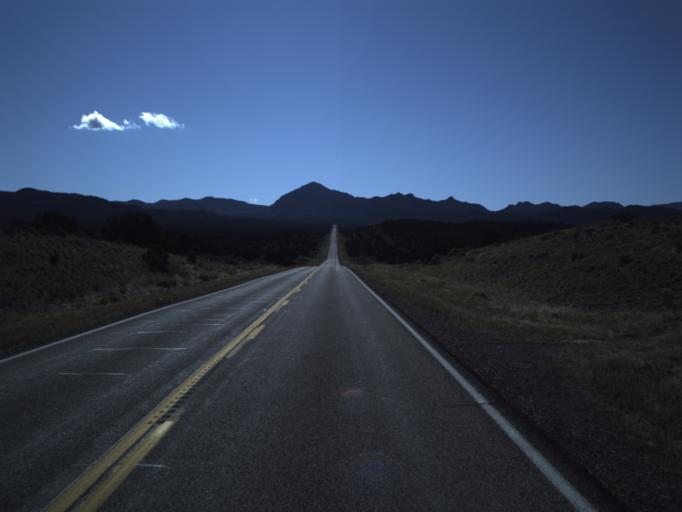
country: US
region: Utah
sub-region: Washington County
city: Enterprise
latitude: 37.6527
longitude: -113.4520
